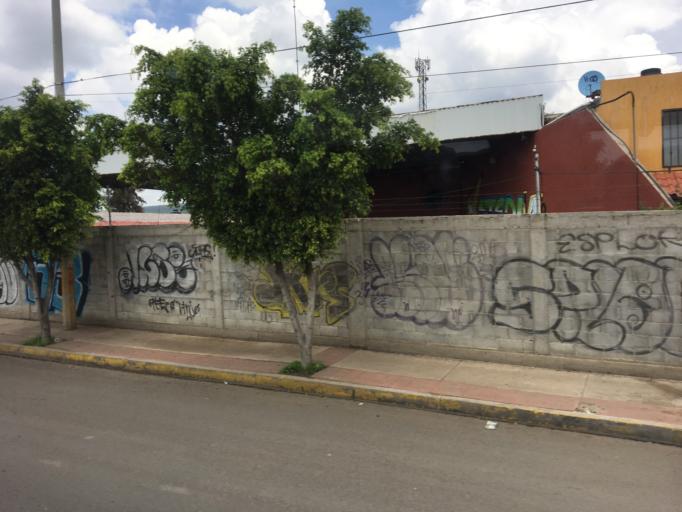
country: MX
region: Guanajuato
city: Irapuato
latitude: 20.7099
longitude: -101.3521
